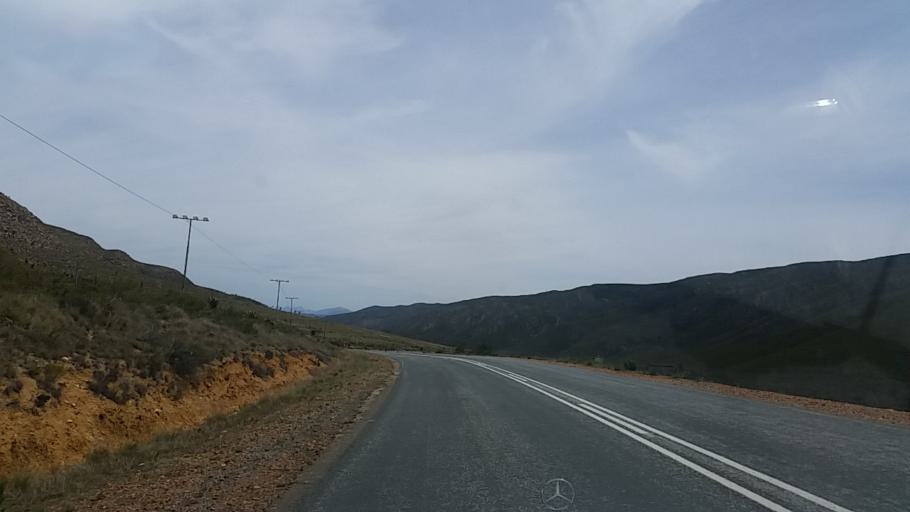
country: ZA
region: Western Cape
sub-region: Eden District Municipality
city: Knysna
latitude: -33.7425
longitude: 23.0083
